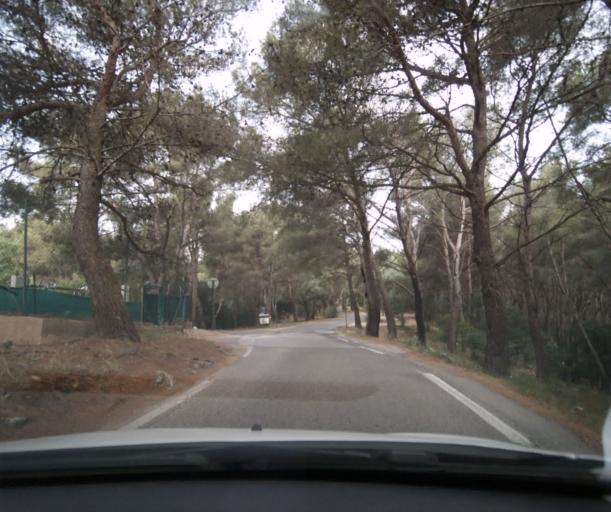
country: FR
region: Provence-Alpes-Cote d'Azur
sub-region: Departement du Var
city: Carqueiranne
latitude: 43.1081
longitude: 6.0880
